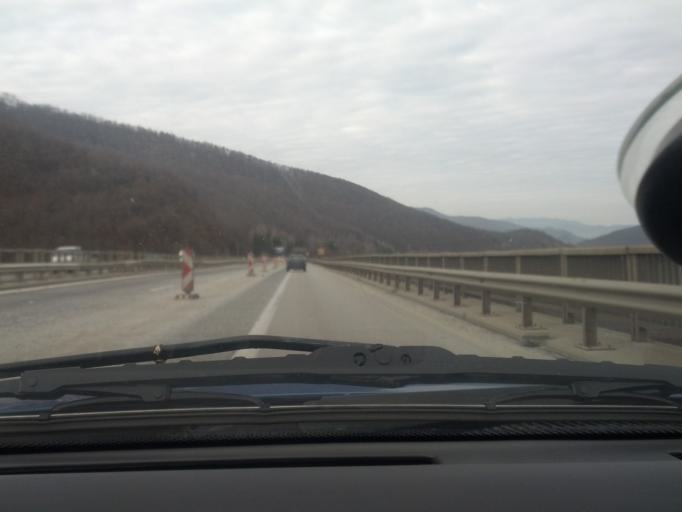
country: BG
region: Sofiya
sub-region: Obshtina Botevgrad
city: Botevgrad
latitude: 42.8081
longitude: 23.8051
